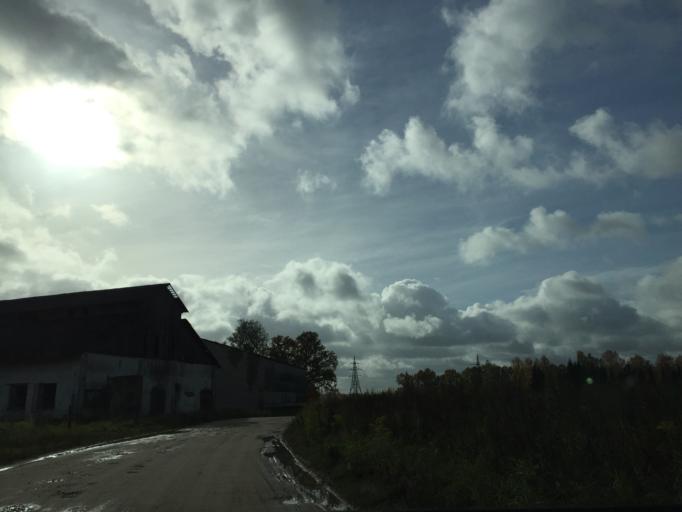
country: LV
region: Lielvarde
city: Lielvarde
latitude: 56.7221
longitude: 24.8308
